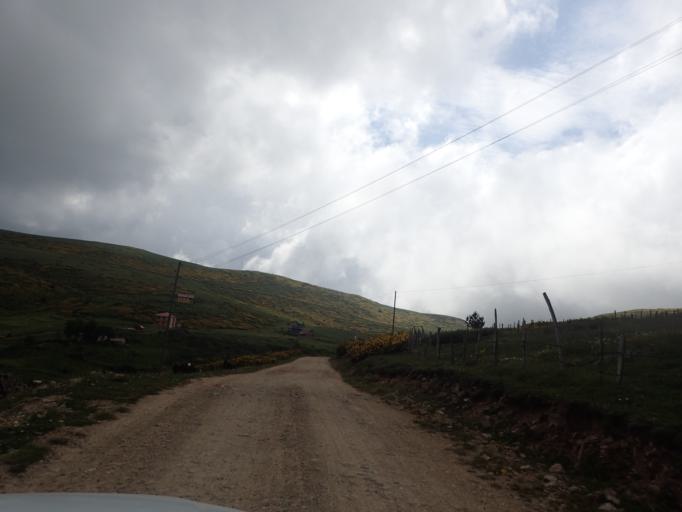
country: TR
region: Ordu
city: Topcam
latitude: 40.6378
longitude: 37.9349
